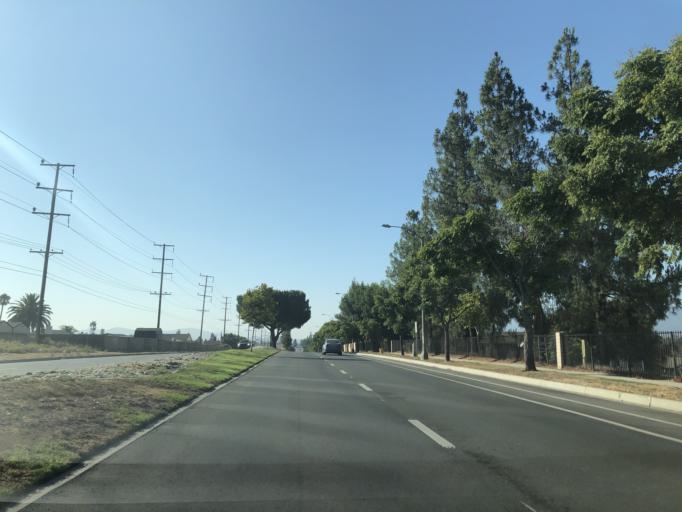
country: US
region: California
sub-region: Riverside County
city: Corona
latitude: 33.9116
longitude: -117.5857
